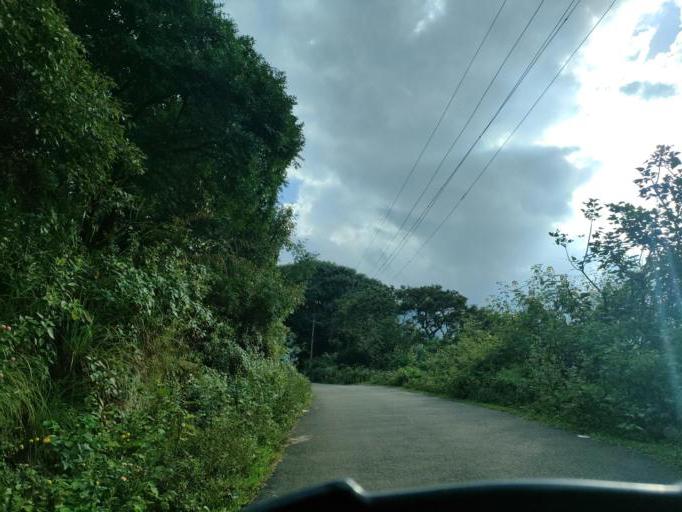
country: IN
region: Tamil Nadu
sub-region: Dindigul
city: Kodaikanal
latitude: 10.2811
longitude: 77.5297
